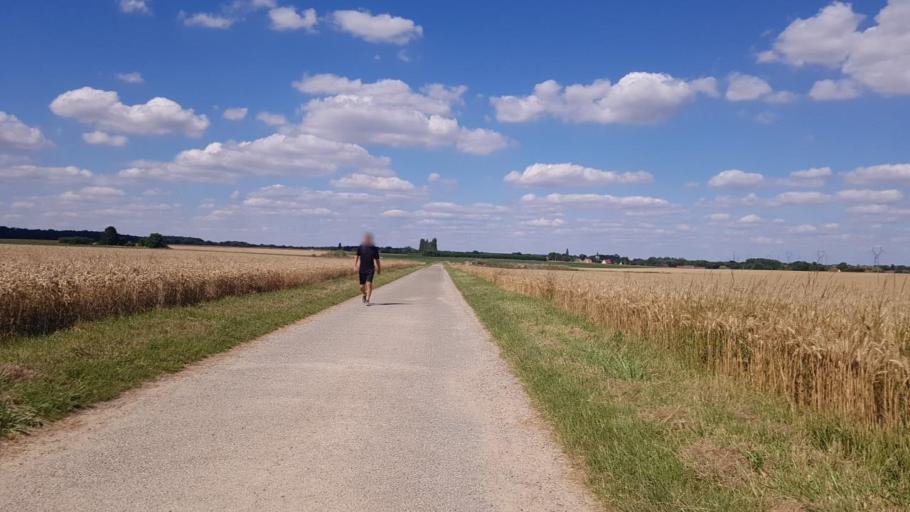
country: FR
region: Picardie
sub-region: Departement de l'Oise
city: Ver-sur-Launette
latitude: 49.0950
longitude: 2.6735
